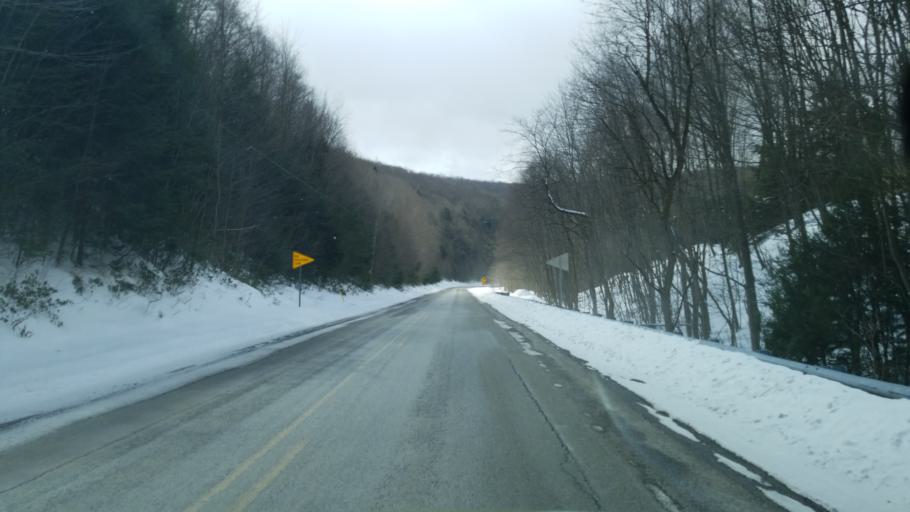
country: US
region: Pennsylvania
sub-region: Clearfield County
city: Shiloh
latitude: 41.2522
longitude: -78.3720
